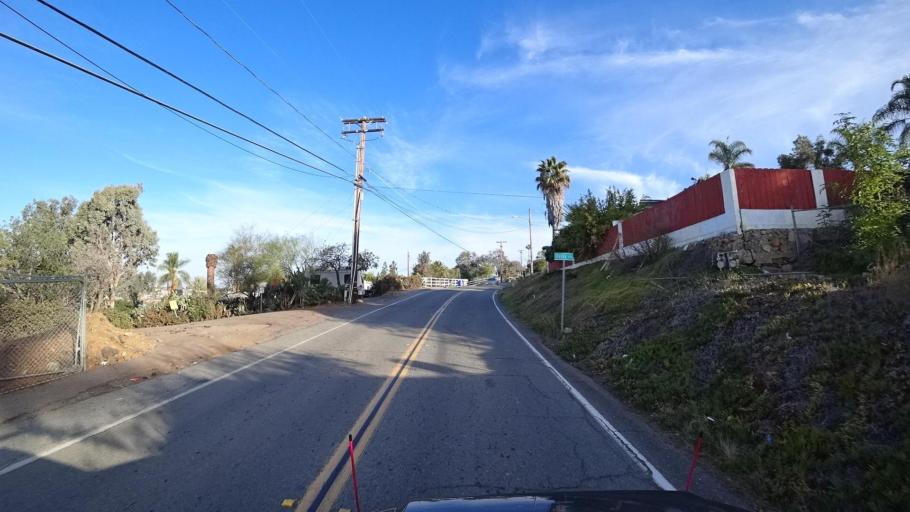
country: US
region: California
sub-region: San Diego County
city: La Presa
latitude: 32.7213
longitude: -117.0088
